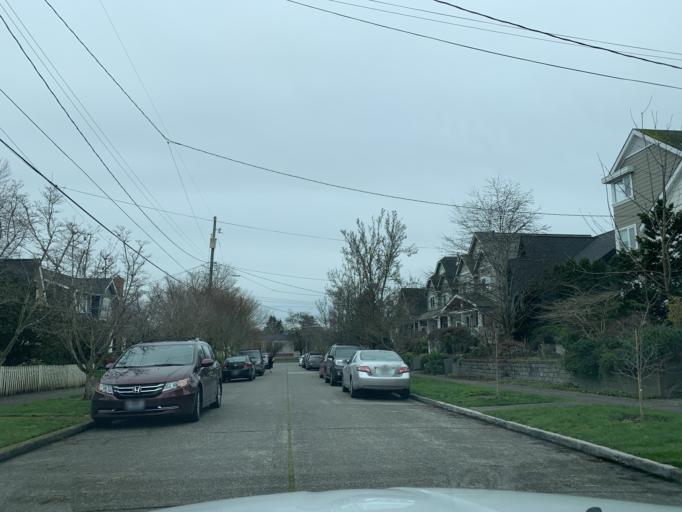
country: US
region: Washington
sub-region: King County
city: Seattle
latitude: 47.6625
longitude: -122.2882
